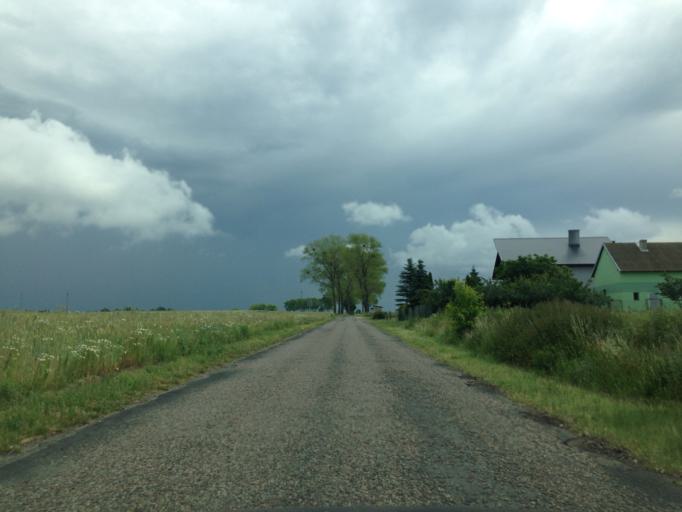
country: PL
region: Kujawsko-Pomorskie
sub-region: Powiat brodnicki
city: Gorzno
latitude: 53.1964
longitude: 19.6168
